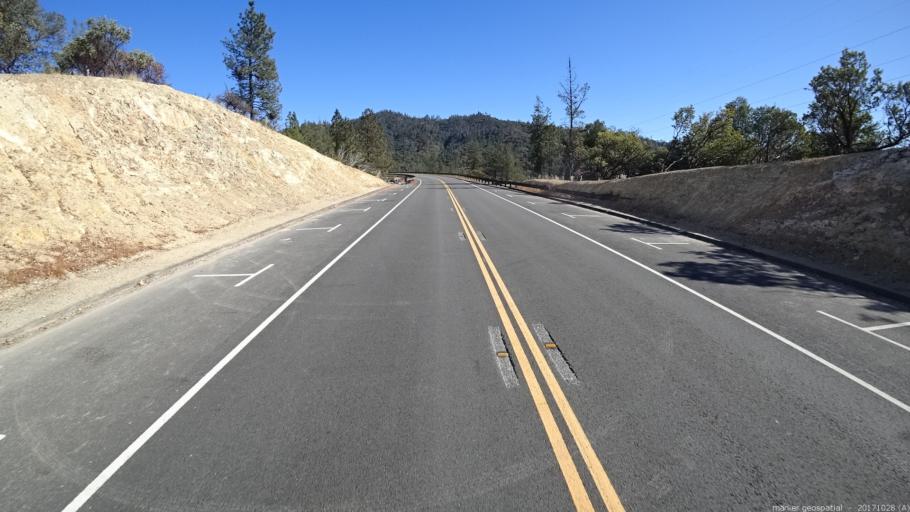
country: US
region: California
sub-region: Shasta County
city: Shasta
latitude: 40.5979
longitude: -122.5434
